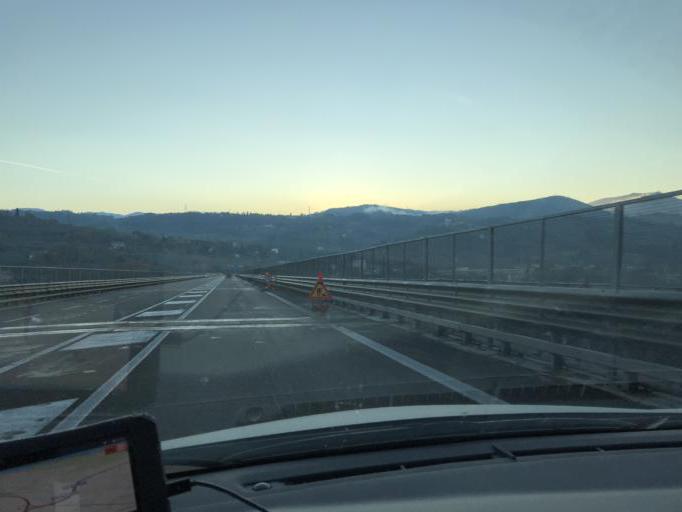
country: IT
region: Umbria
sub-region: Provincia di Terni
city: Terni
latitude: 42.5840
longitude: 12.6739
